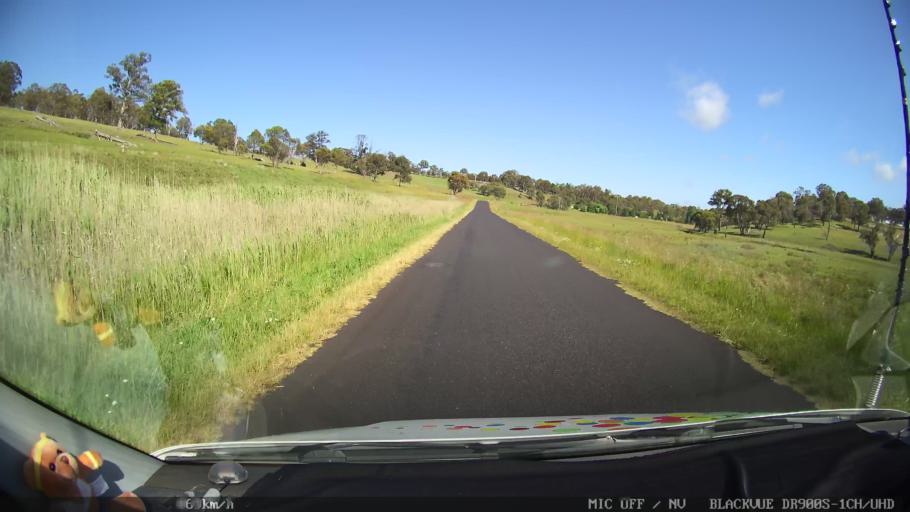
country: AU
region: New South Wales
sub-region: Guyra
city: Guyra
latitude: -30.1159
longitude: 151.6865
